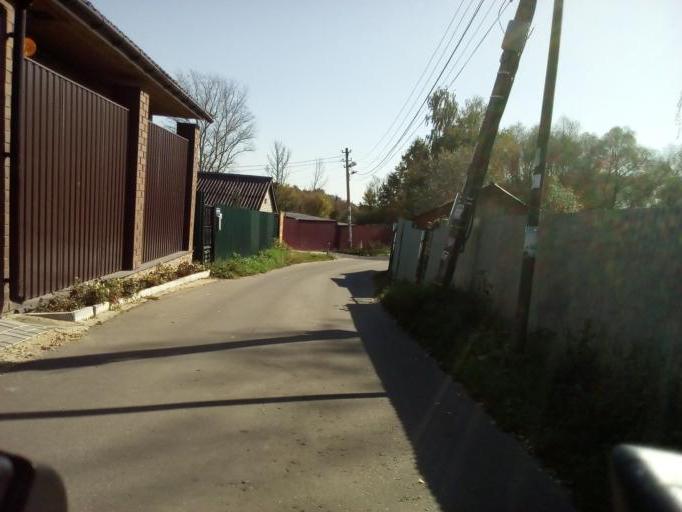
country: RU
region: Moskovskaya
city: Ramenskoye
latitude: 55.5469
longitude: 38.2881
